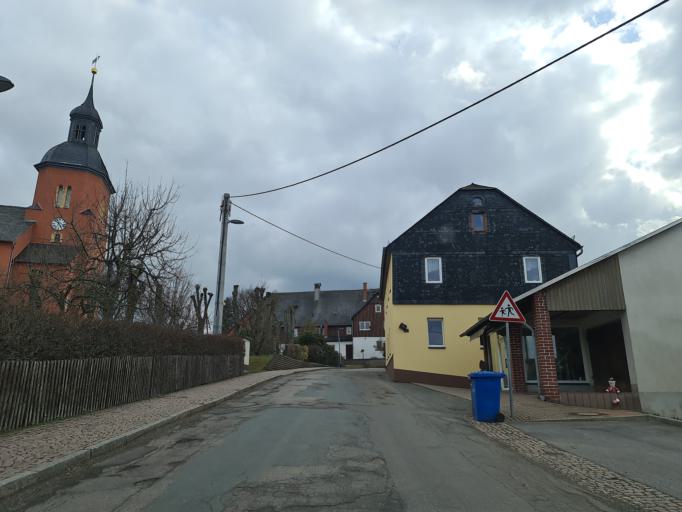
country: DE
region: Saxony
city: Reinsdorf
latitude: 50.7043
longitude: 12.6167
